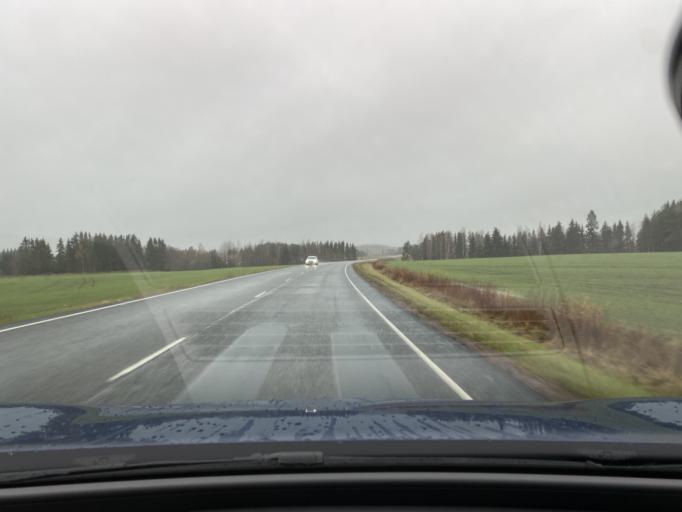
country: FI
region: Varsinais-Suomi
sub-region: Loimaa
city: Alastaro
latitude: 60.8819
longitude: 22.9806
